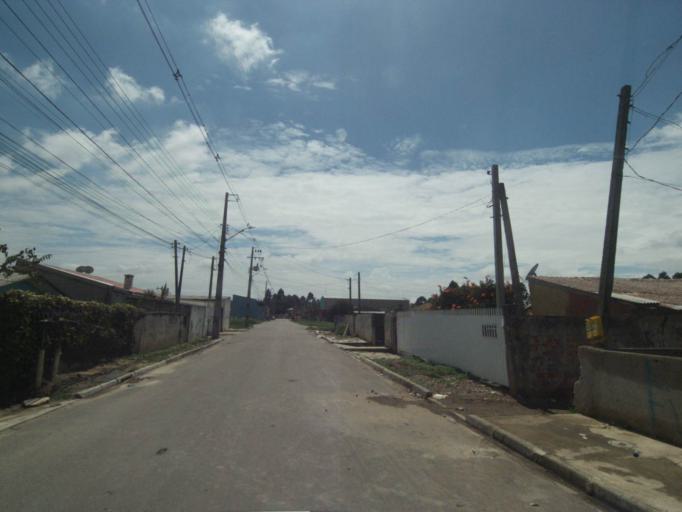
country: BR
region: Parana
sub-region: Pinhais
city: Pinhais
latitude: -25.4744
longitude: -49.1898
